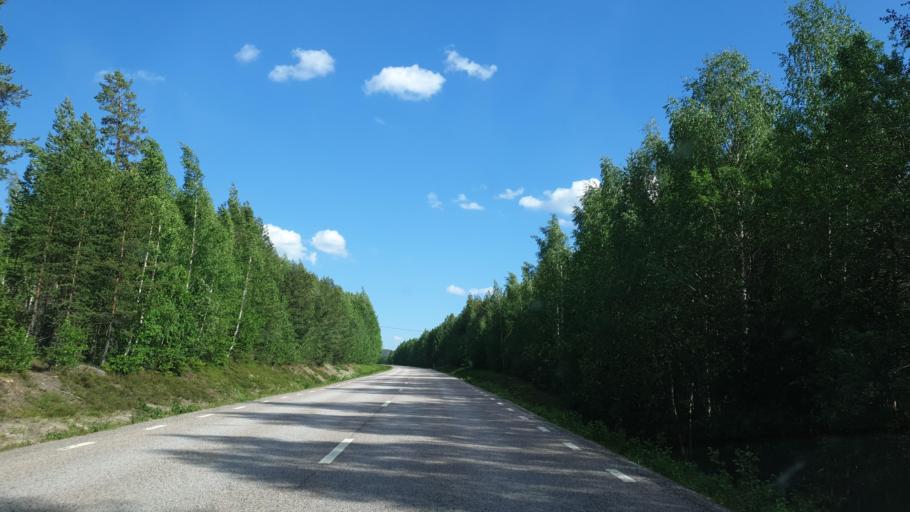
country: SE
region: Norrbotten
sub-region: Alvsbyns Kommun
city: AElvsbyn
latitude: 65.8046
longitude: 20.6193
